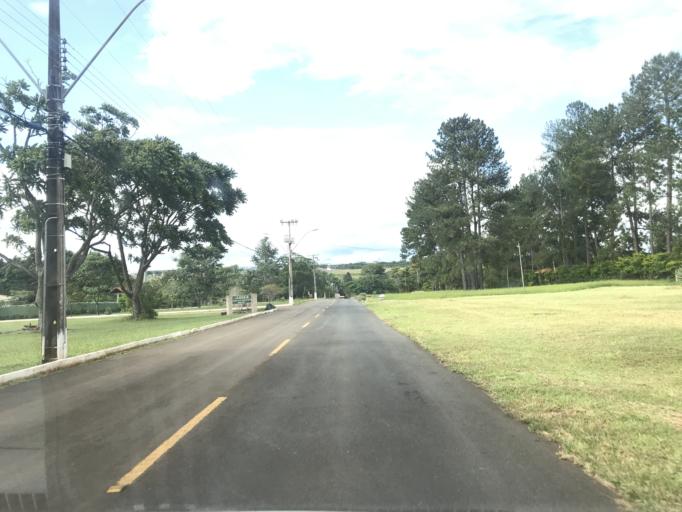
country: BR
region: Federal District
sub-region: Brasilia
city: Brasilia
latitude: -15.8887
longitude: -47.9178
